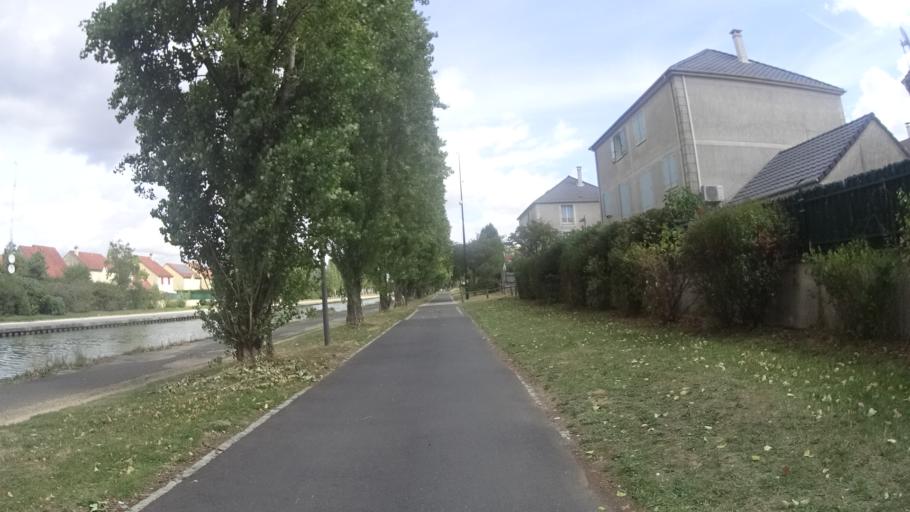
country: FR
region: Ile-de-France
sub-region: Departement de Seine-Saint-Denis
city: Les Pavillons-sous-Bois
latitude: 48.9160
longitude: 2.5040
